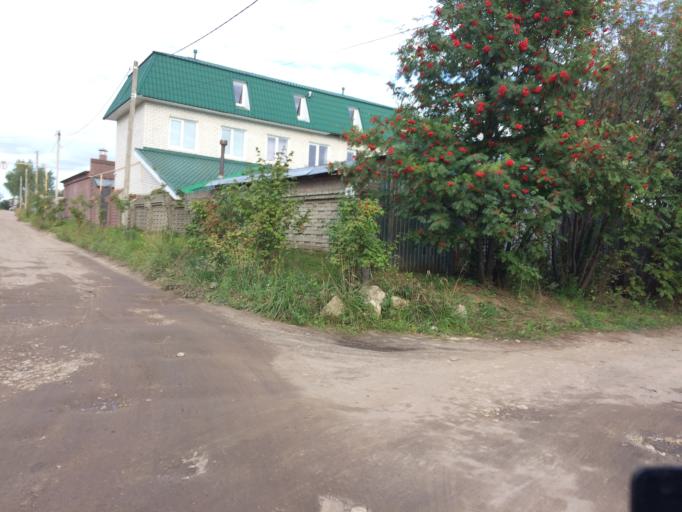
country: RU
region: Mariy-El
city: Yoshkar-Ola
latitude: 56.6541
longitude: 48.0130
